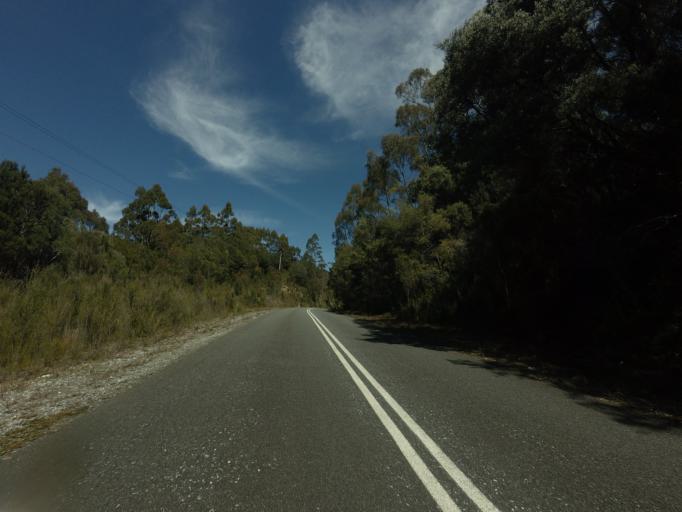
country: AU
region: Tasmania
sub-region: West Coast
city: Queenstown
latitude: -42.7727
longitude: 146.0425
